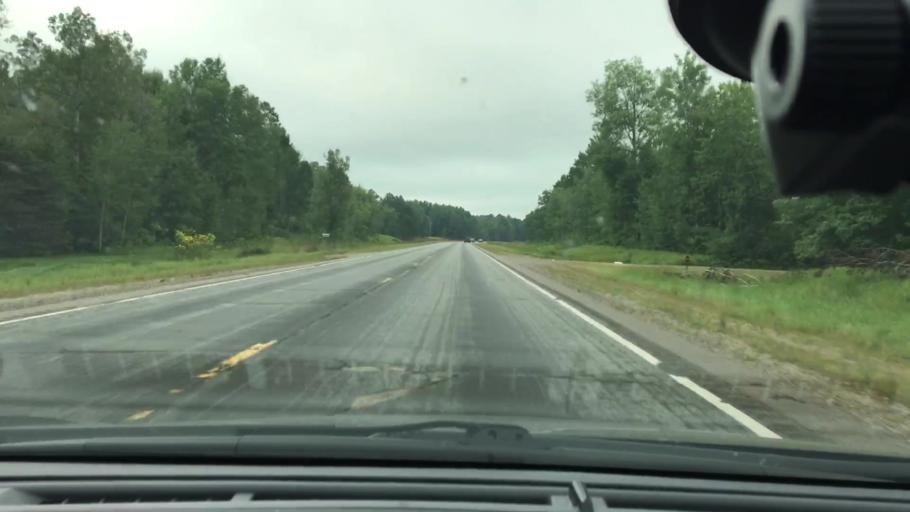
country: US
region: Minnesota
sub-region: Crow Wing County
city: Cross Lake
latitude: 46.6740
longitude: -93.9521
